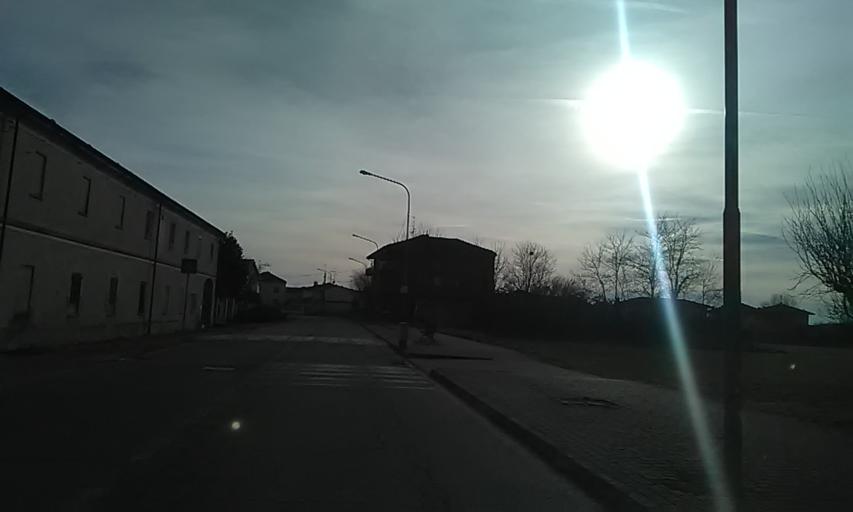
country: IT
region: Piedmont
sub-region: Provincia di Vercelli
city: Stroppiana
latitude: 45.2349
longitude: 8.4559
